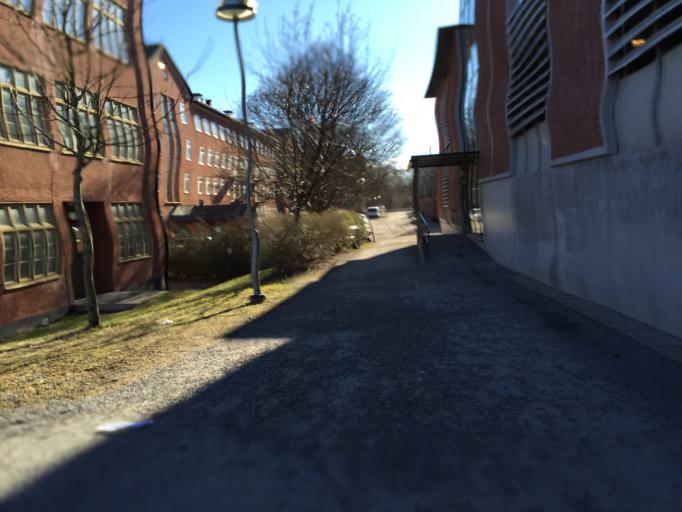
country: SE
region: Stockholm
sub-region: Stockholms Kommun
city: Bromma
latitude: 59.3598
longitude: 17.9011
